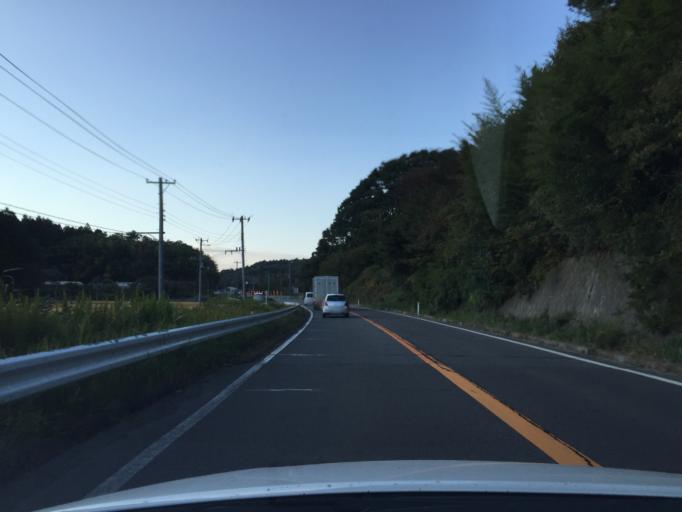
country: JP
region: Fukushima
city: Ishikawa
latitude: 37.2664
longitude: 140.5546
